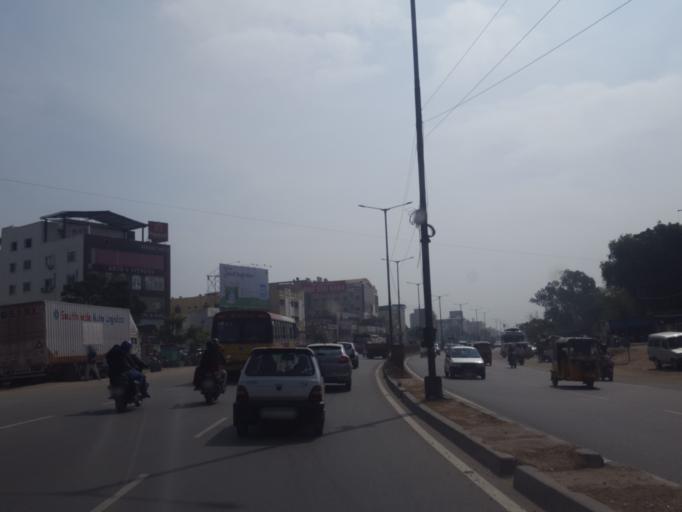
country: IN
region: Telangana
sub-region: Medak
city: Serilingampalle
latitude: 17.5029
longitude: 78.3113
